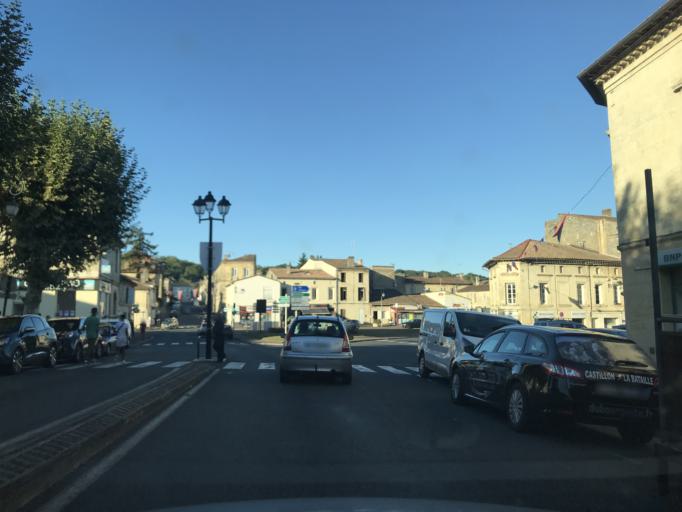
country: FR
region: Aquitaine
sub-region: Departement de la Gironde
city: Mouliets-et-Villemartin
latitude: 44.8539
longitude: -0.0427
